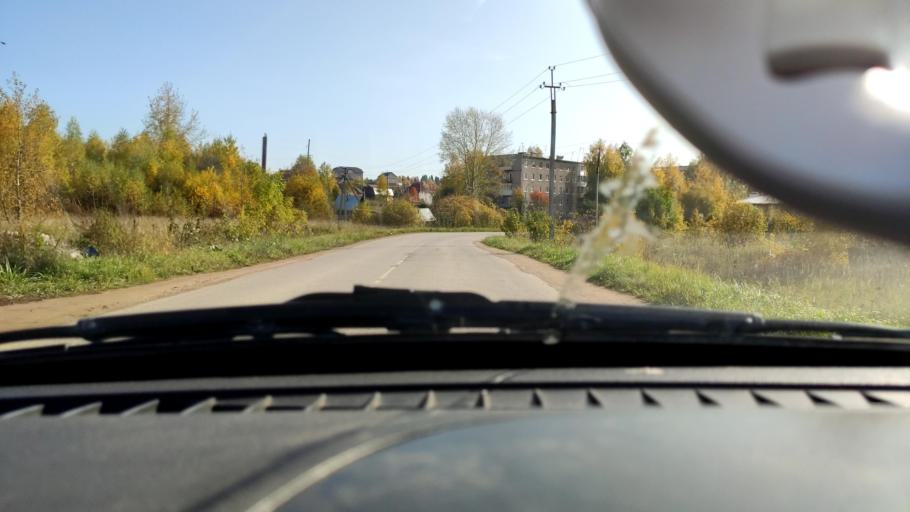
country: RU
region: Perm
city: Overyata
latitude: 58.0852
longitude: 55.8756
